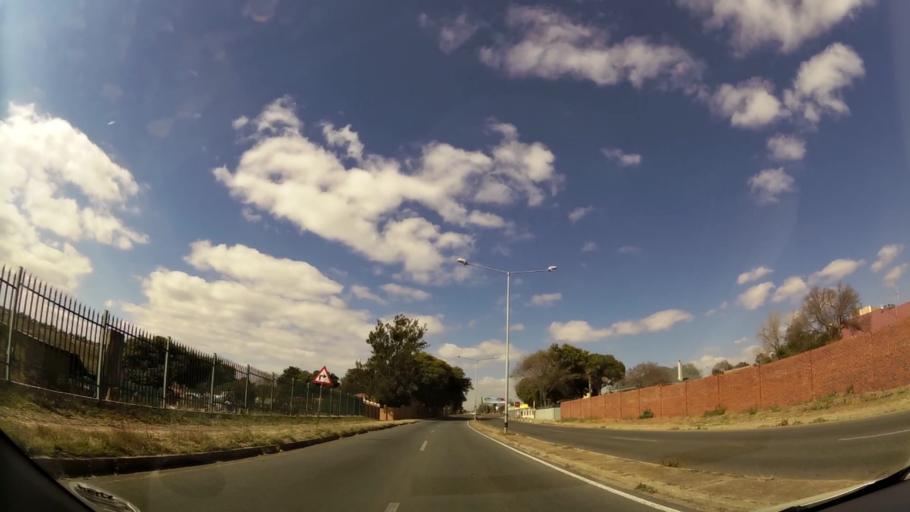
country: ZA
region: Gauteng
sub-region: West Rand District Municipality
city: Krugersdorp
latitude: -26.1069
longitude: 27.7838
